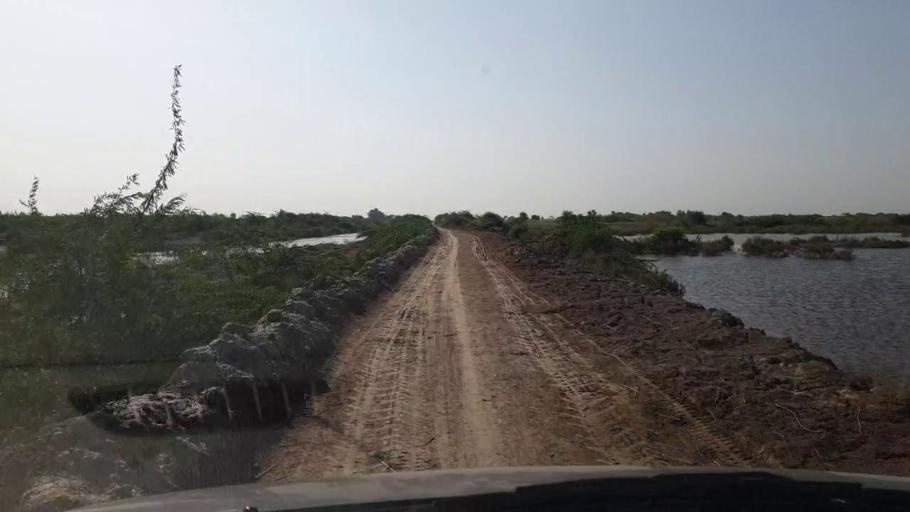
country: PK
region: Sindh
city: Kadhan
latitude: 24.6032
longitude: 69.0743
